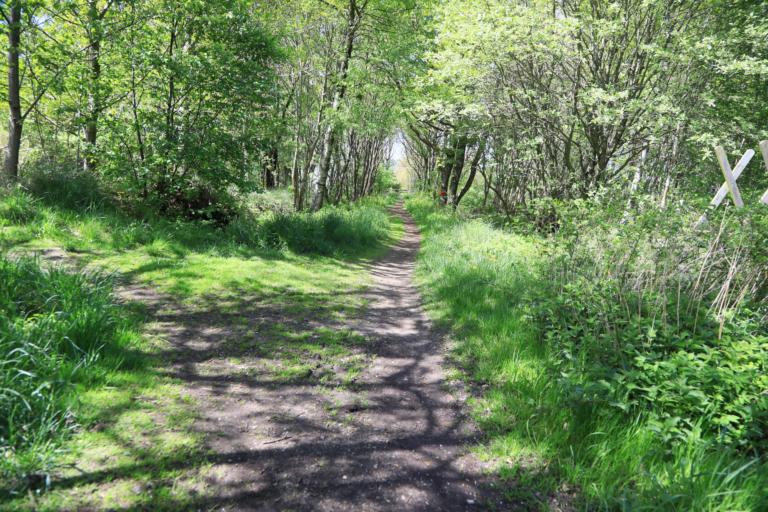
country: SE
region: Halland
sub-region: Varbergs Kommun
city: Varberg
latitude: 57.1170
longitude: 12.2989
